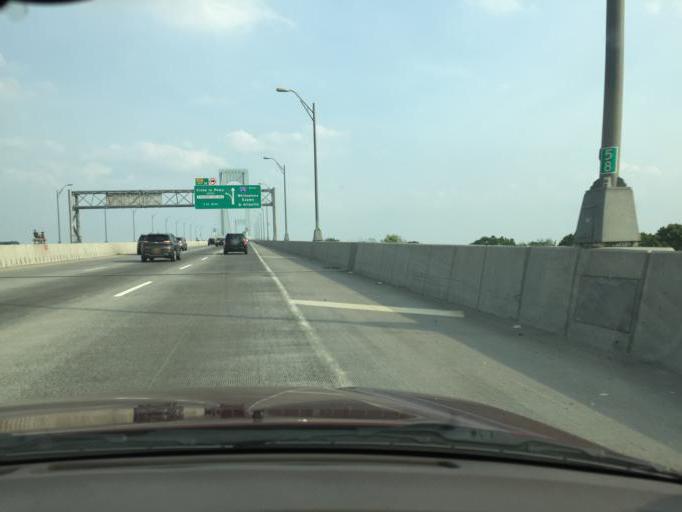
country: US
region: New York
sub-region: Bronx
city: The Bronx
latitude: 40.8098
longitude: -73.8349
